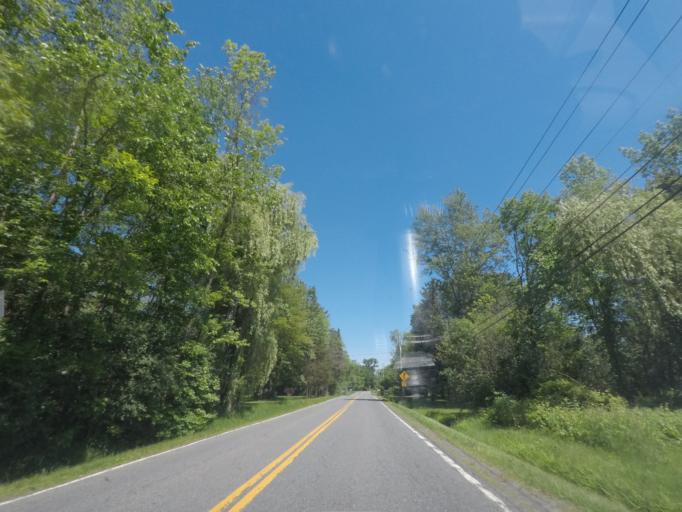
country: US
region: New York
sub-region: Schenectady County
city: East Glenville
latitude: 42.8805
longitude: -73.8650
